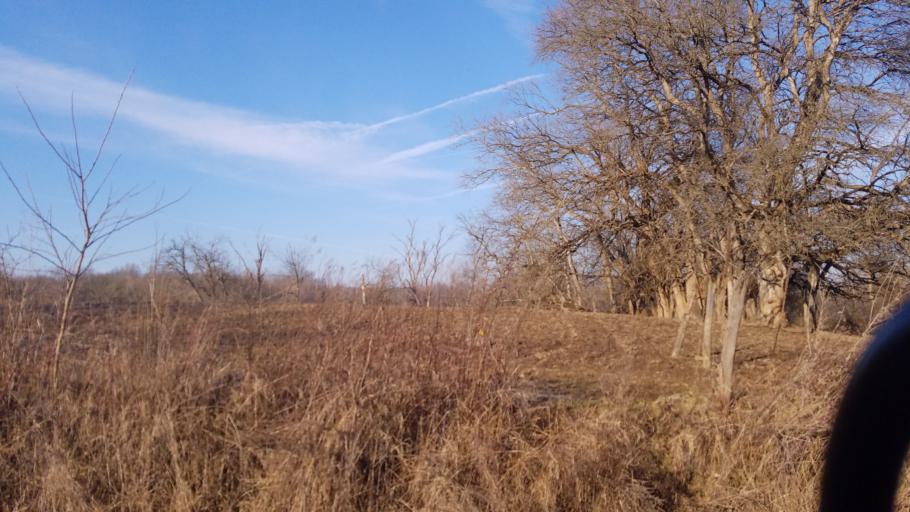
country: US
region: Ohio
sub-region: Knox County
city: Fredericktown
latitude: 40.5091
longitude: -82.6442
